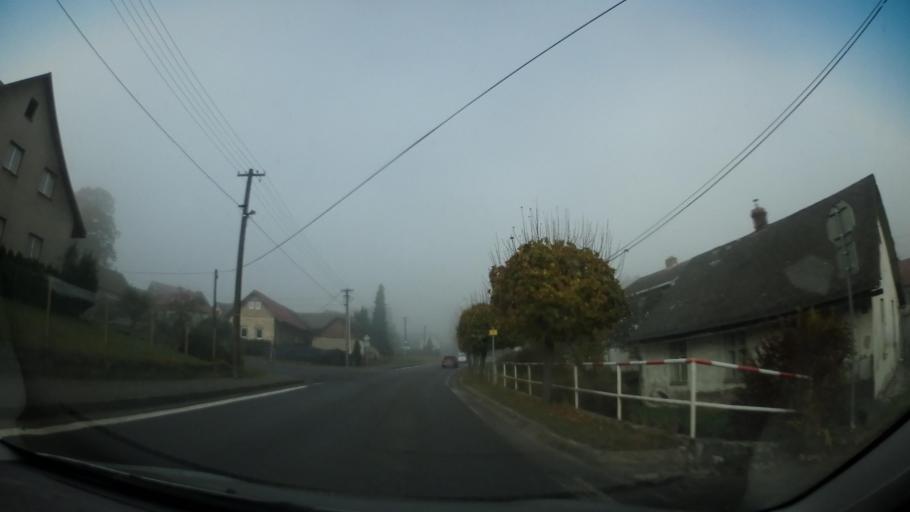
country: CZ
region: Vysocina
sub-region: Okres Zd'ar nad Sazavou
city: Nove Mesto na Morave
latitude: 49.4743
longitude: 16.0592
